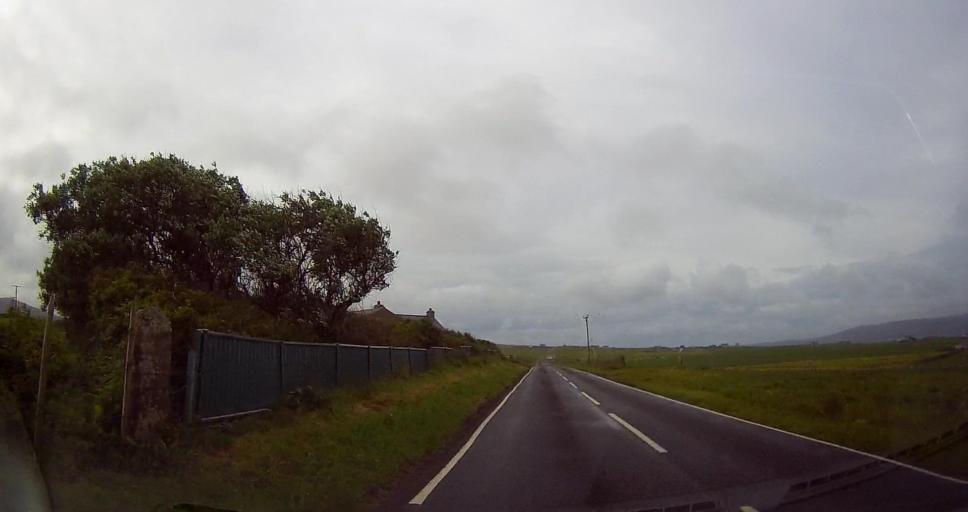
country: GB
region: Scotland
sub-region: Orkney Islands
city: Stromness
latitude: 58.9670
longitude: -3.2261
